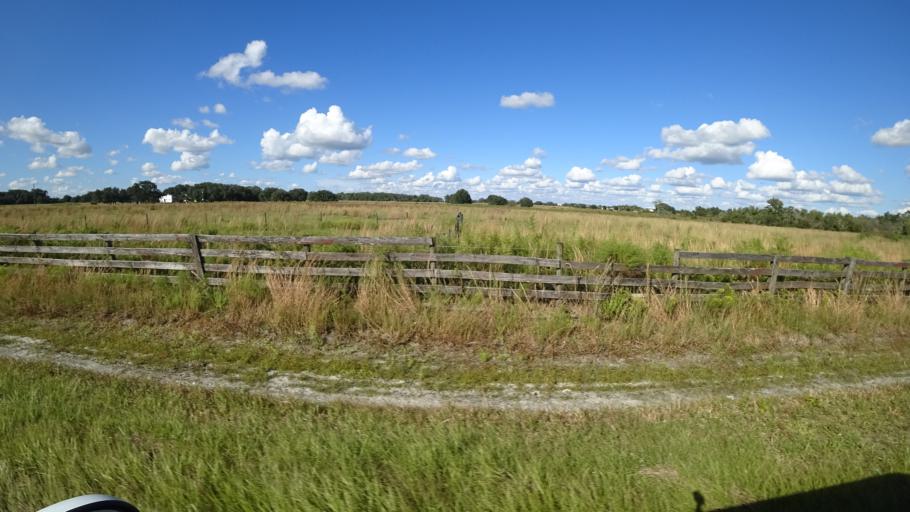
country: US
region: Florida
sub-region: Sarasota County
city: Warm Mineral Springs
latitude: 27.2739
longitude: -82.2014
